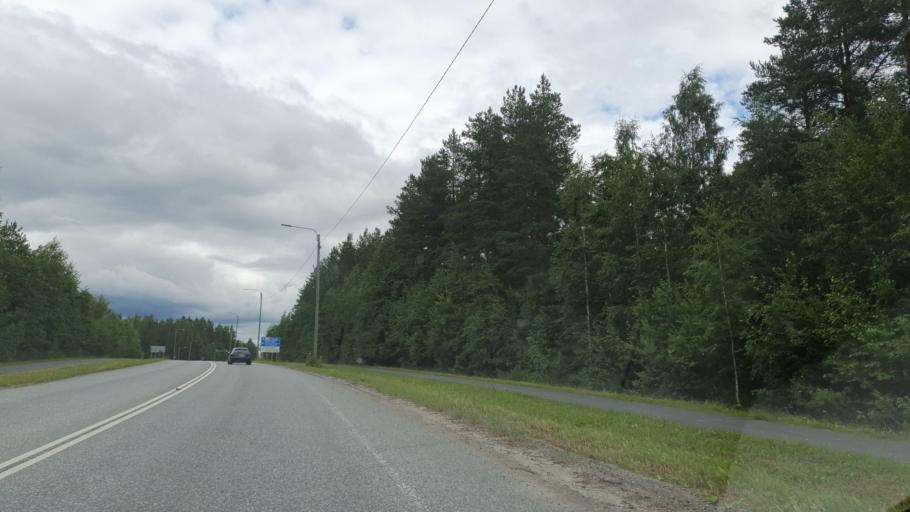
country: FI
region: Northern Savo
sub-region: Ylae-Savo
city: Iisalmi
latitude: 63.5199
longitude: 27.2393
